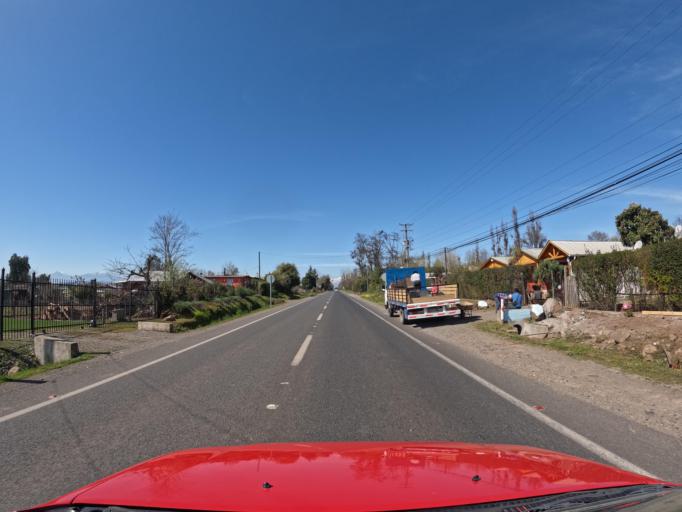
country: CL
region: Maule
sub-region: Provincia de Curico
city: Teno
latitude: -34.9635
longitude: -71.0688
